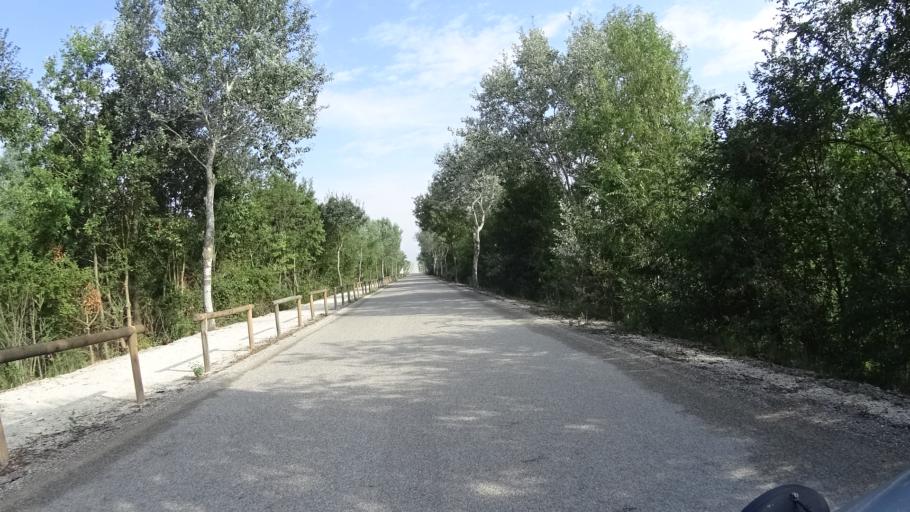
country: IT
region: Veneto
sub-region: Provincia di Venezia
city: Bibione
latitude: 45.6341
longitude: 12.9518
